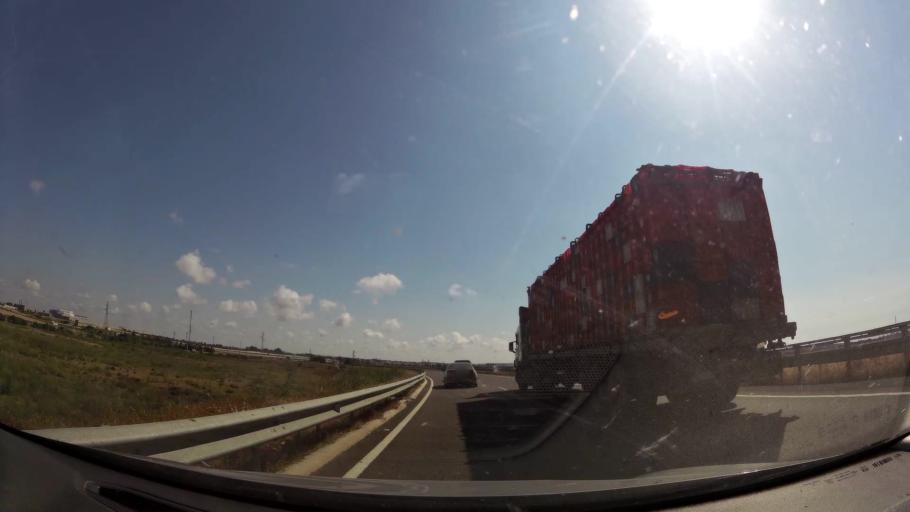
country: MA
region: Rabat-Sale-Zemmour-Zaer
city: Skhirat
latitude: 33.8753
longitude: -7.0138
